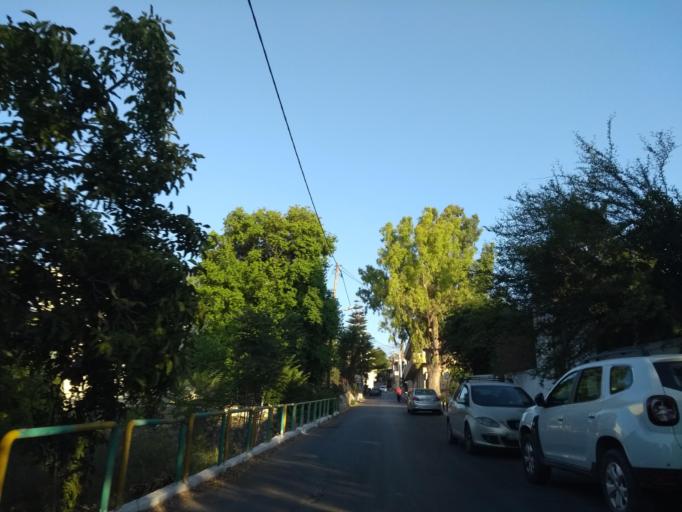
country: GR
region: Crete
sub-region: Nomos Chanias
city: Kalivai
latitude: 35.4088
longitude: 24.1978
